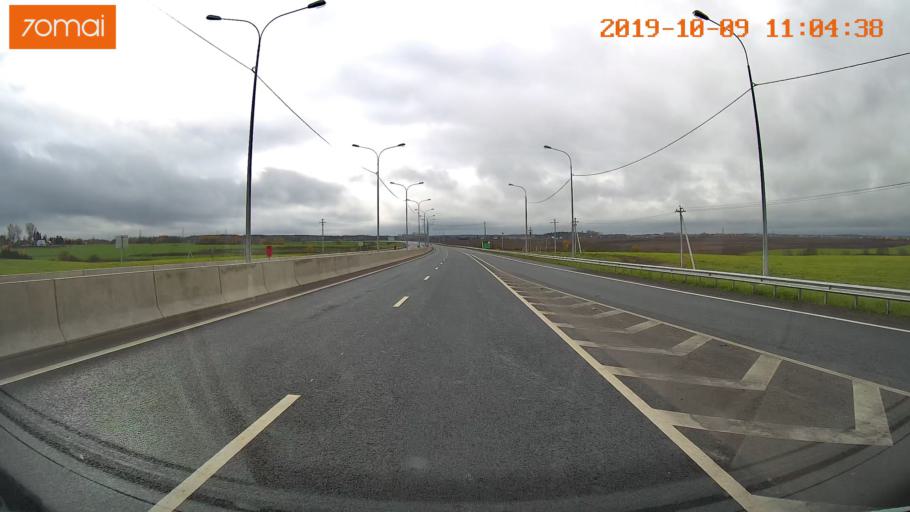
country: RU
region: Vologda
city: Vologda
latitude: 59.2101
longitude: 39.7657
